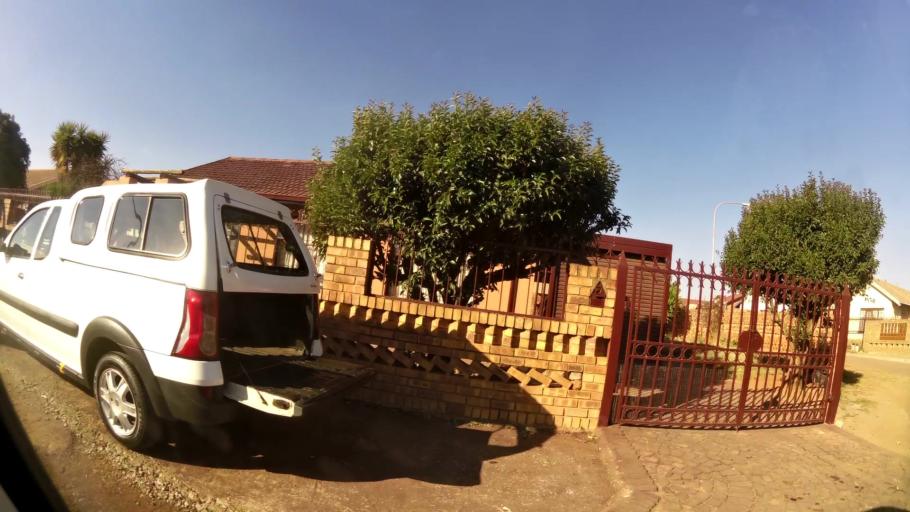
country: ZA
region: Gauteng
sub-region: City of Tshwane Metropolitan Municipality
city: Cullinan
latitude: -25.7147
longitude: 28.3883
